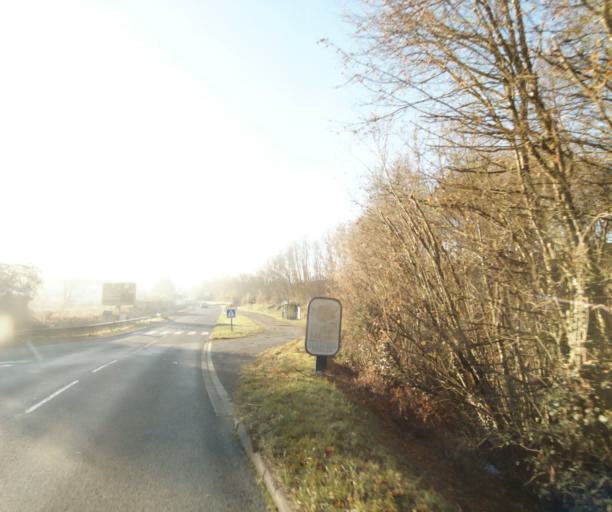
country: FR
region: Poitou-Charentes
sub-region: Departement de la Charente-Maritime
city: Saintes
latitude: 45.7622
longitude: -0.6175
